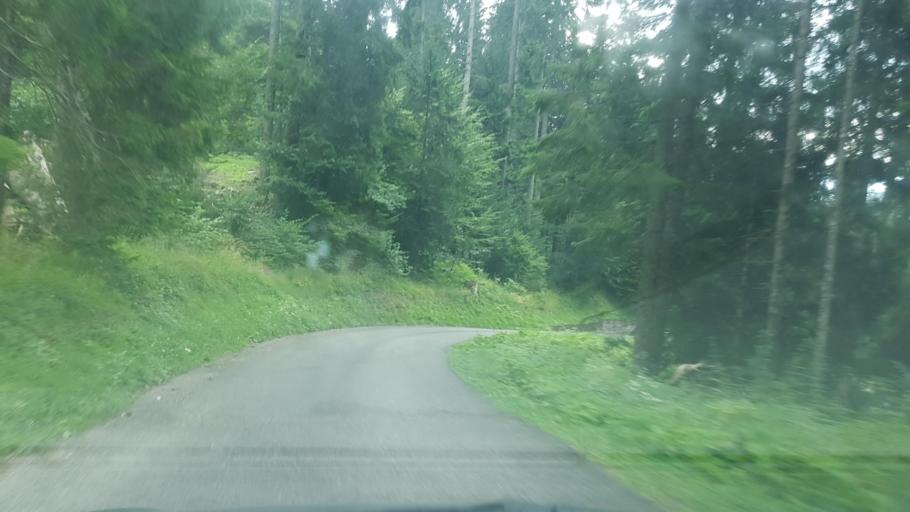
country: IT
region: Friuli Venezia Giulia
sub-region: Provincia di Udine
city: Rigolato
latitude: 46.5536
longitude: 12.8272
